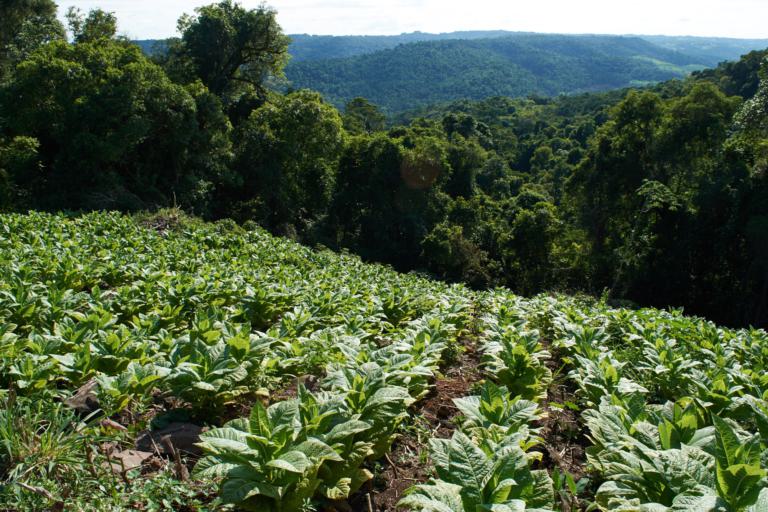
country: AR
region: Misiones
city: Dos de Mayo
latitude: -26.9058
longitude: -54.5650
